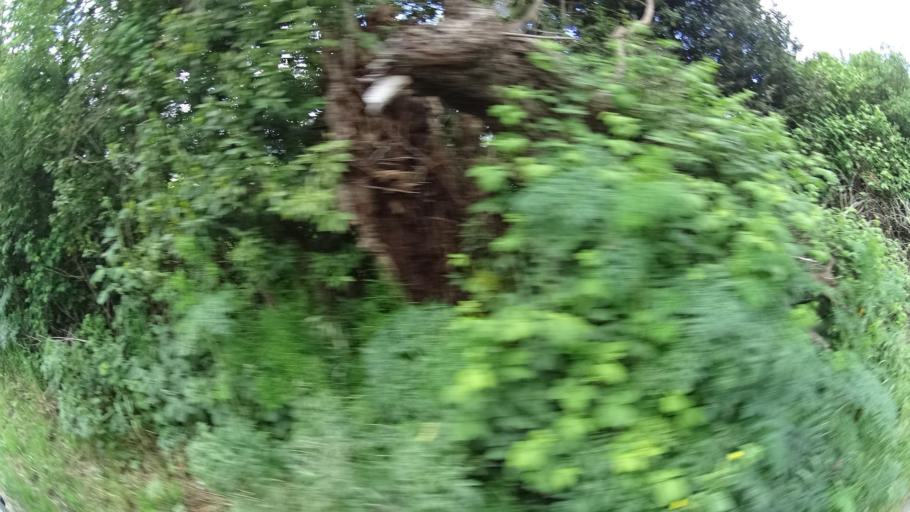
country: US
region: California
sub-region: Humboldt County
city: Blue Lake
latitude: 40.8935
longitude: -124.0033
